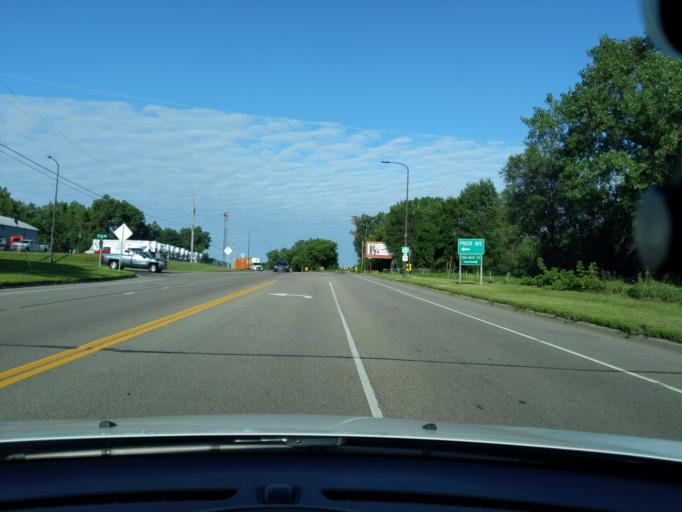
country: US
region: Minnesota
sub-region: Ramsey County
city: Falcon Heights
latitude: 44.9688
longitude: -93.1816
